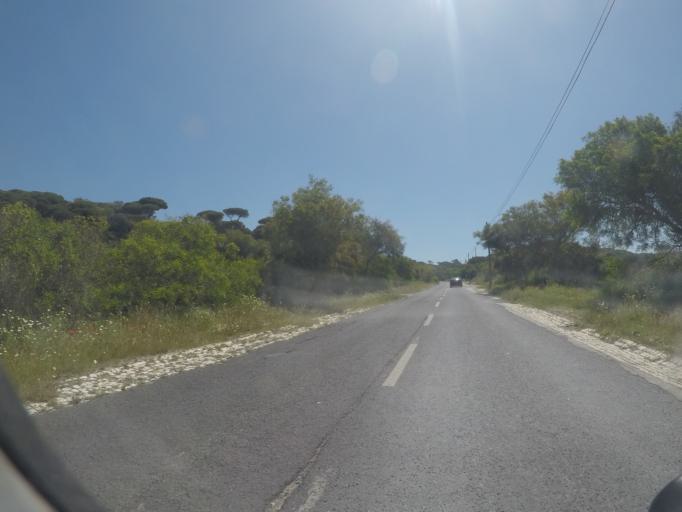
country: PT
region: Setubal
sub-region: Almada
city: Charneca
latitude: 38.6089
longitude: -9.2048
